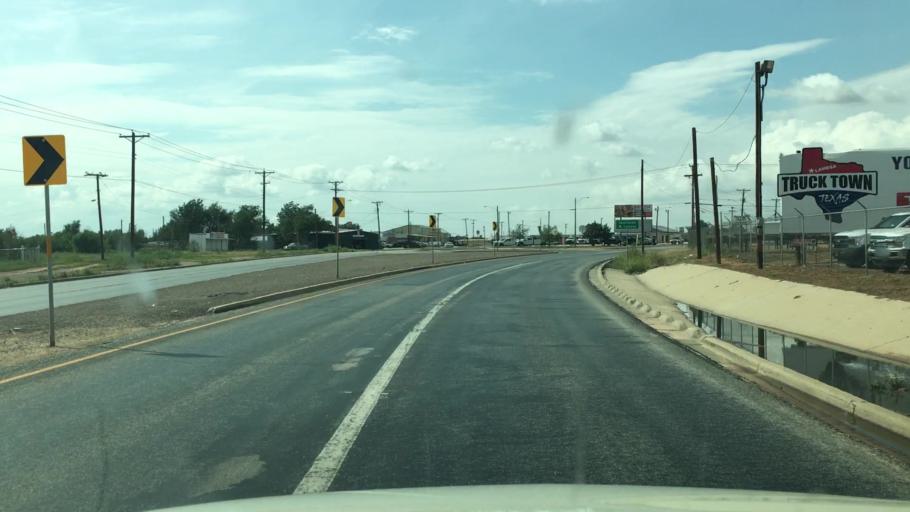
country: US
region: Texas
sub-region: Dawson County
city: Lamesa
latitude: 32.7196
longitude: -101.9446
